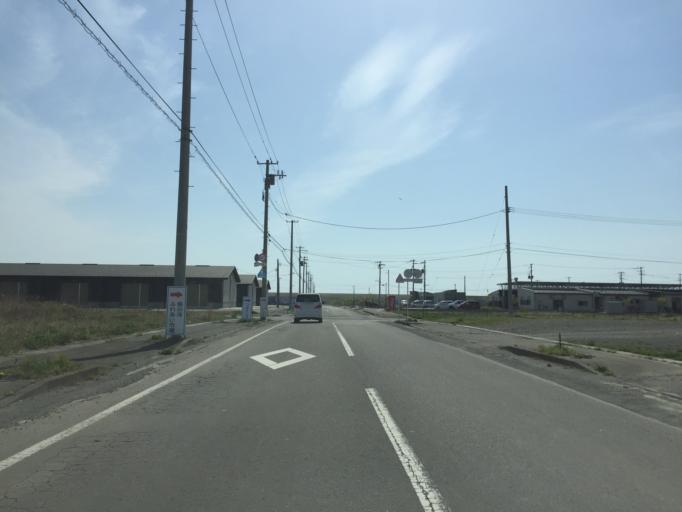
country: JP
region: Miyagi
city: Watari
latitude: 38.0402
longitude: 140.9155
